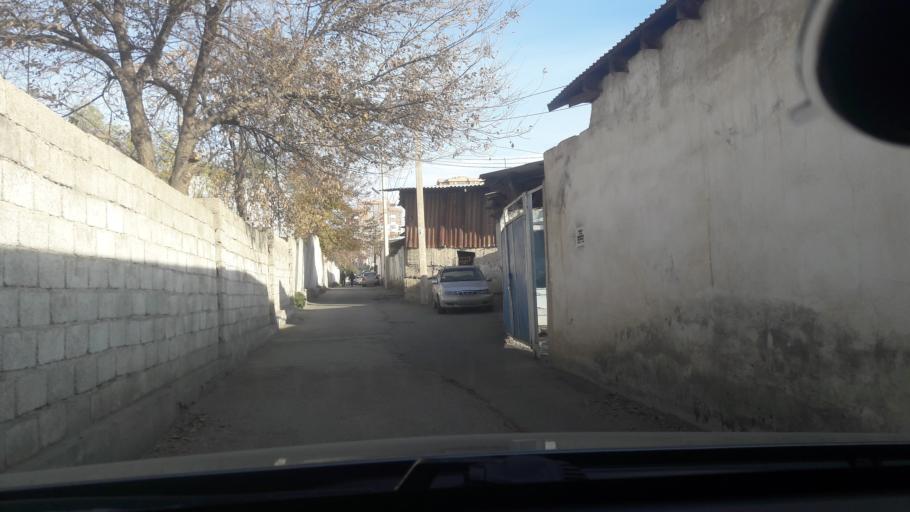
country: TJ
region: Dushanbe
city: Dushanbe
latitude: 38.5815
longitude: 68.7596
